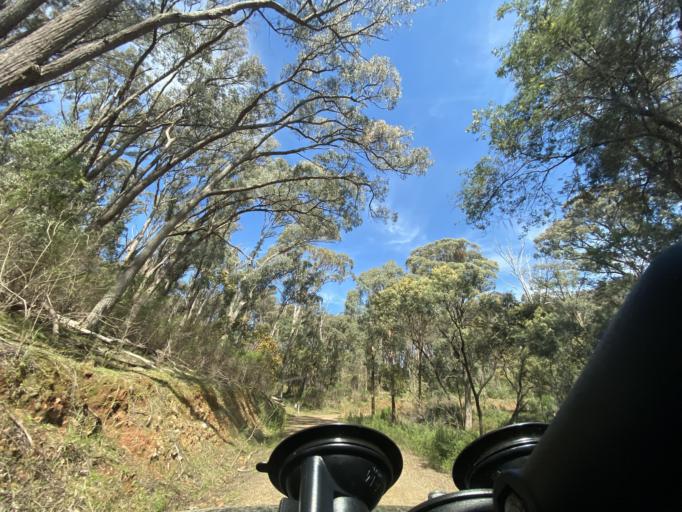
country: AU
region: Victoria
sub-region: Mansfield
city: Mansfield
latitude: -36.8150
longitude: 146.1027
